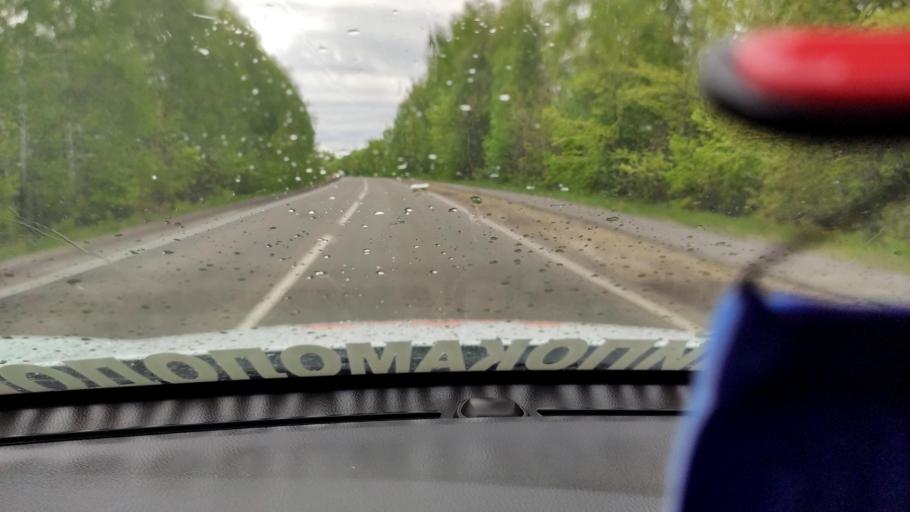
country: RU
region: Voronezj
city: Imeni Pervogo Maya
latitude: 50.7482
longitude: 39.3872
